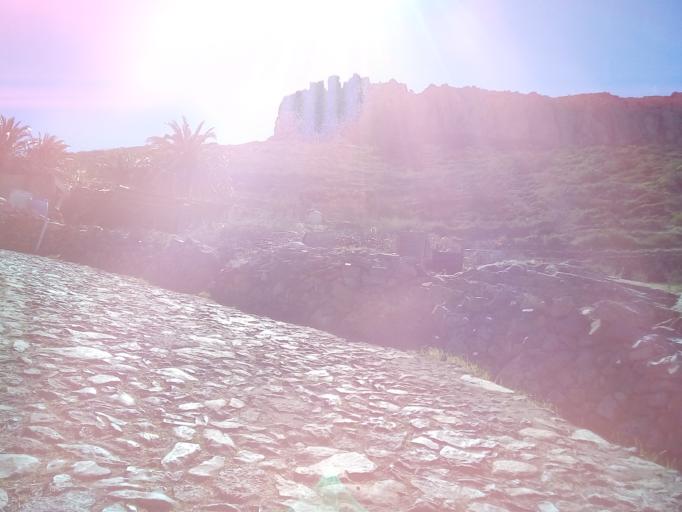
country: ES
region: Canary Islands
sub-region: Provincia de Santa Cruz de Tenerife
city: Alajero
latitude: 28.1036
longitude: -17.2751
